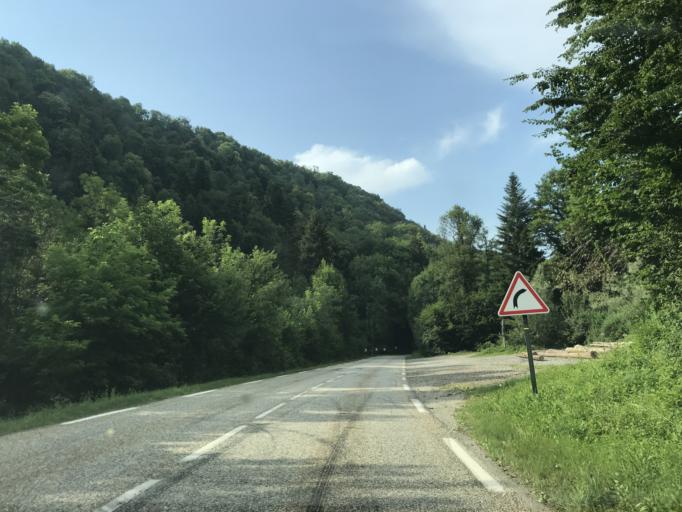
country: FR
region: Rhone-Alpes
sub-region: Departement de l'Isere
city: Allevard
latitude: 45.4261
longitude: 6.0925
